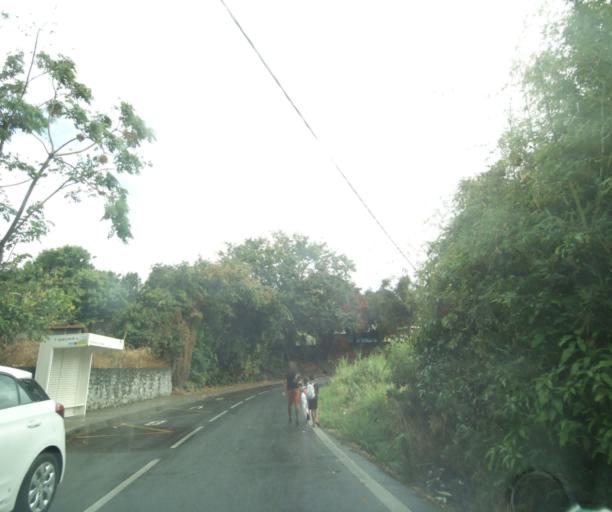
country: RE
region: Reunion
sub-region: Reunion
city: Saint-Paul
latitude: -21.0071
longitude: 55.3217
